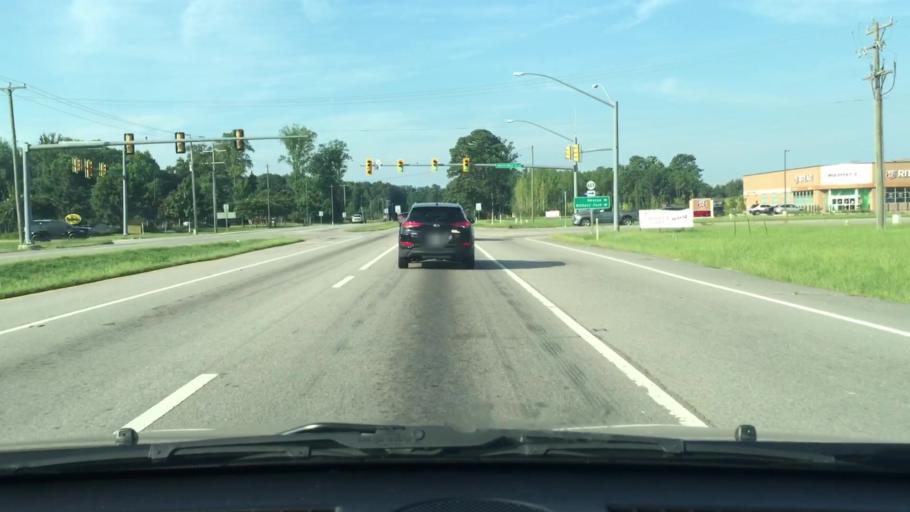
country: US
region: Virginia
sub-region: Isle of Wight County
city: Carrollton
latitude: 36.9523
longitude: -76.5312
